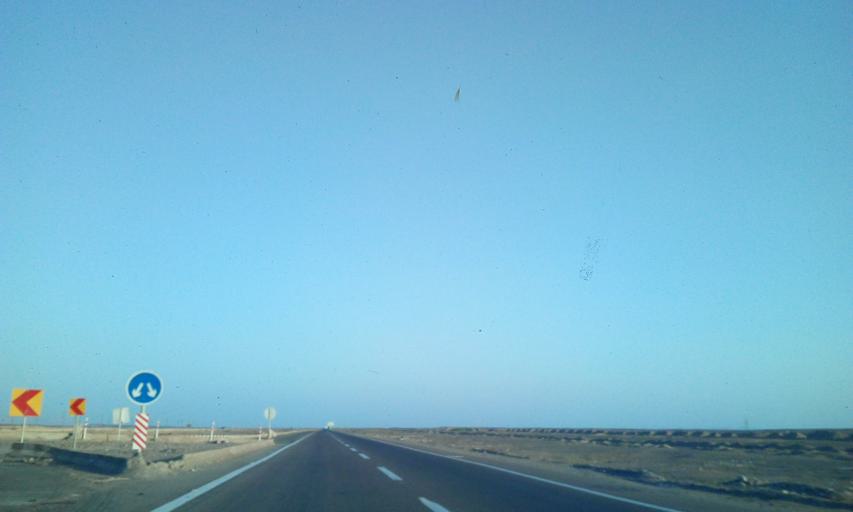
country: EG
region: South Sinai
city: Tor
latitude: 28.0626
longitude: 33.2688
